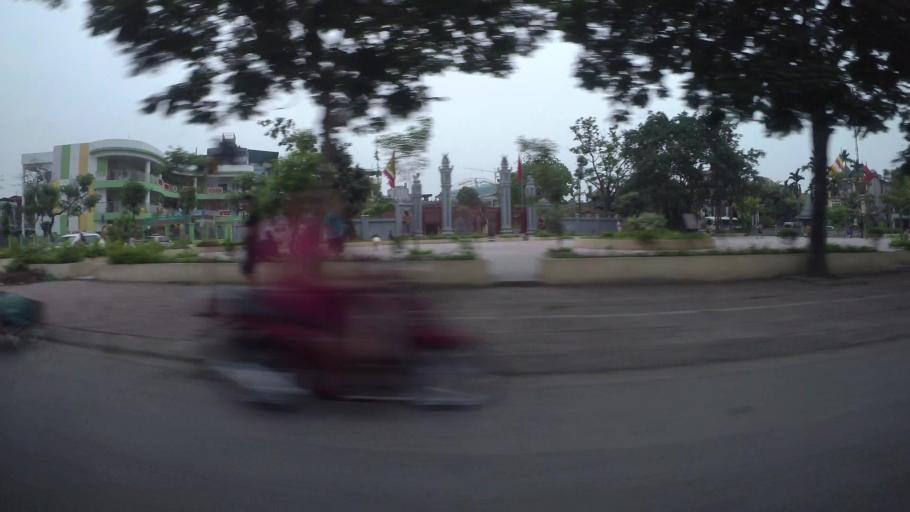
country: VN
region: Ha Noi
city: Trau Quy
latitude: 21.0403
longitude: 105.8979
